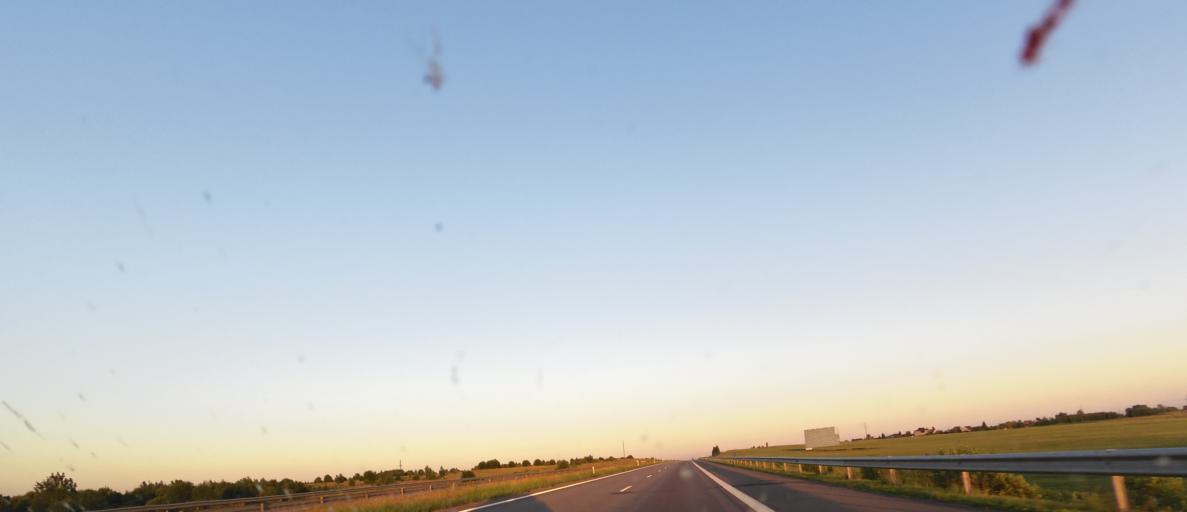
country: LT
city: Sirvintos
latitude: 54.8882
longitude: 25.0581
